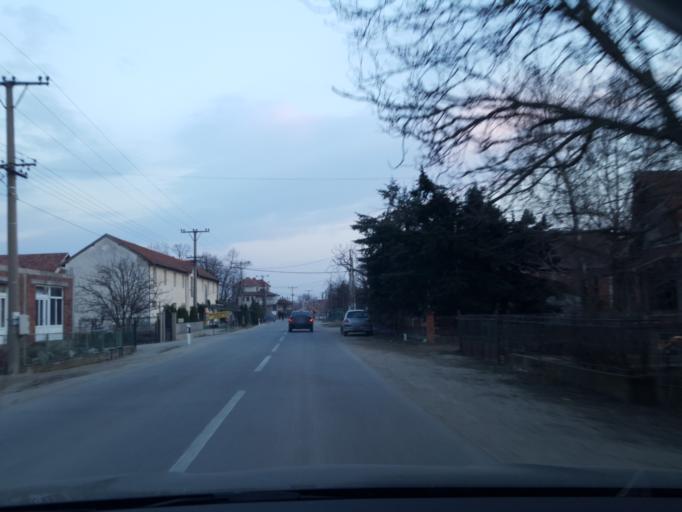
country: RS
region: Central Serbia
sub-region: Nisavski Okrug
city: Aleksinac
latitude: 43.5015
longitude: 21.7022
